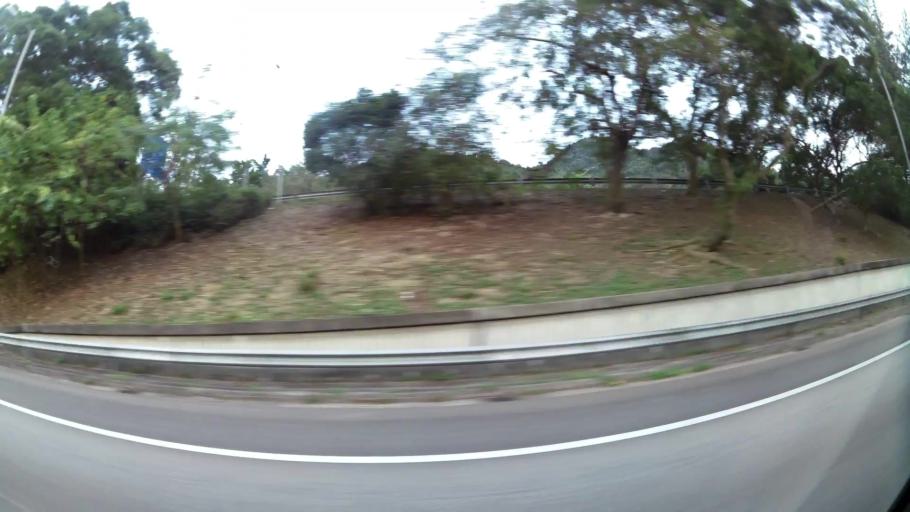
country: HK
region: Sha Tin
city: Sha Tin
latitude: 22.3962
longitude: 114.2104
